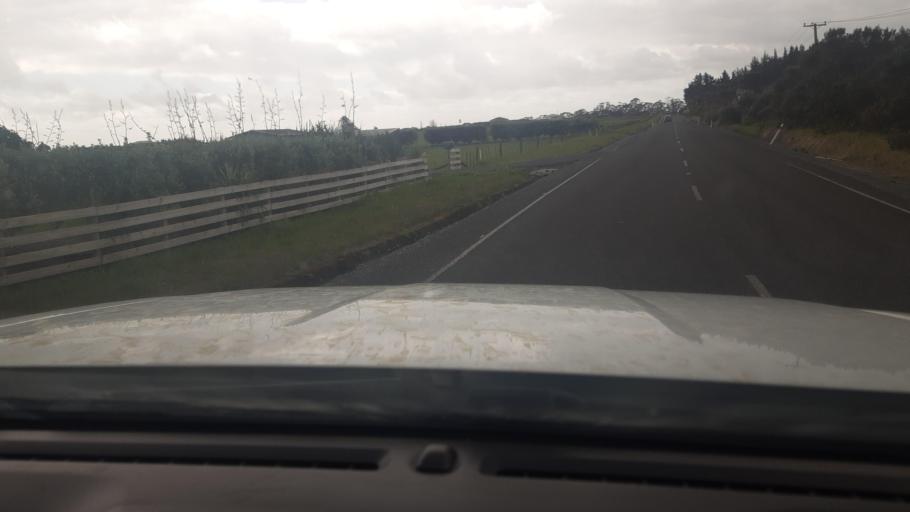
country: NZ
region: Northland
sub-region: Far North District
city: Kaitaia
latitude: -35.0413
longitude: 173.3152
